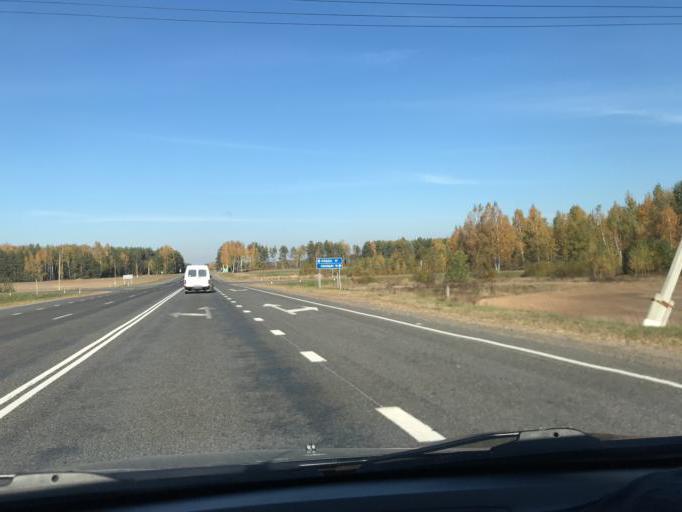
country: BY
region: Gomel
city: Parychy
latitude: 52.6741
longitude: 29.3614
